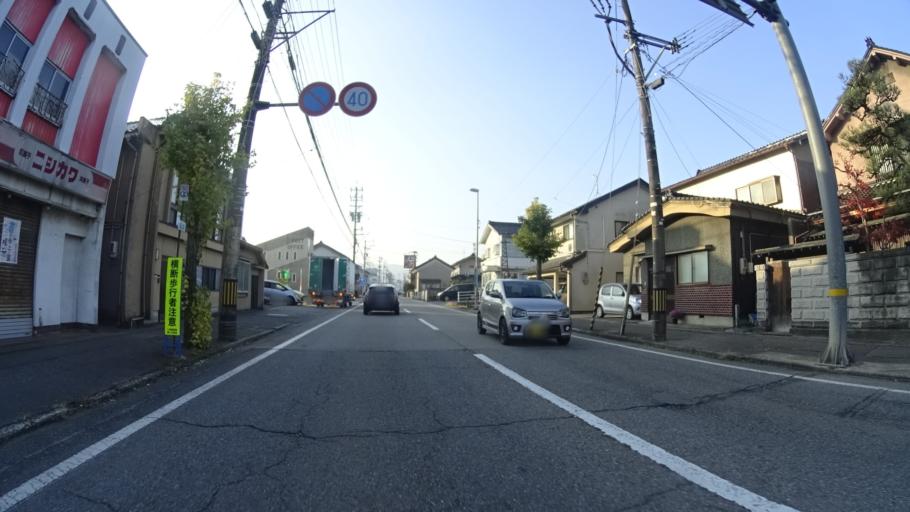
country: JP
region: Ishikawa
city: Nanao
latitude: 37.0392
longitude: 136.9693
